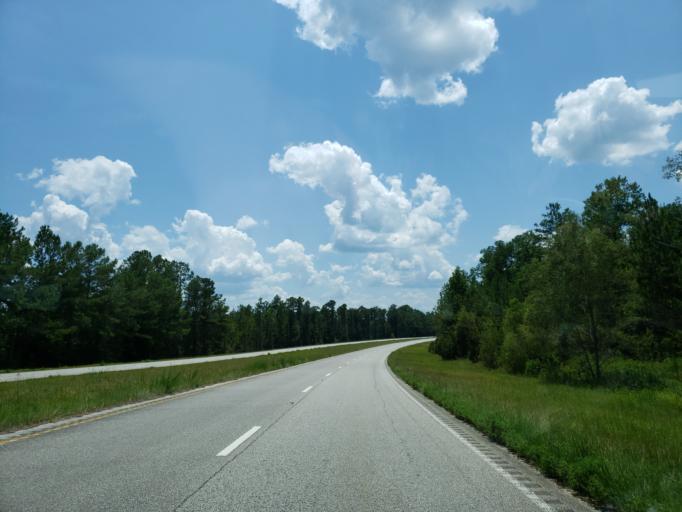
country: US
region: Mississippi
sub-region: Wayne County
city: Belmont
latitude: 31.3698
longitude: -88.4872
